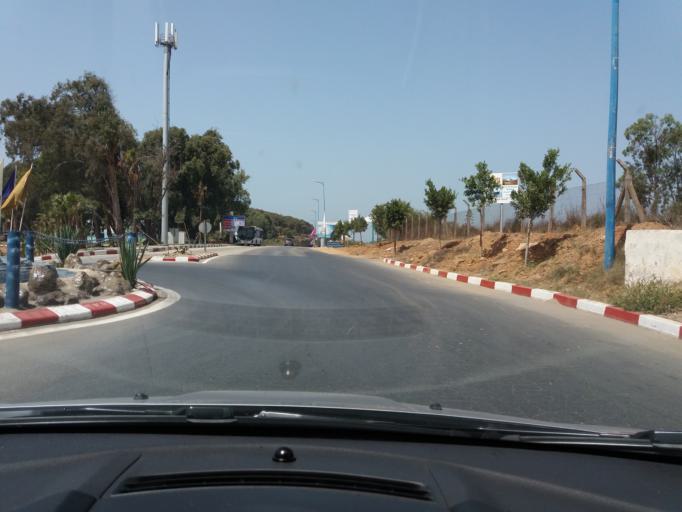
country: MA
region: Gharb-Chrarda-Beni Hssen
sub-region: Kenitra Province
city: Kenitra
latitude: 34.2703
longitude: -6.6404
